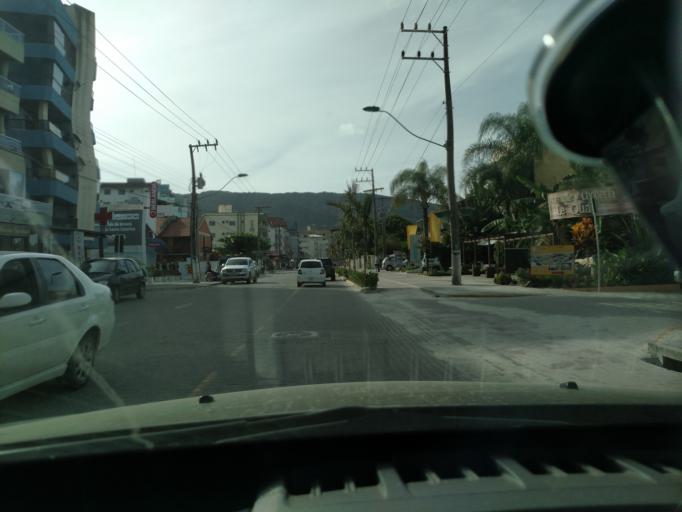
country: BR
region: Santa Catarina
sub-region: Porto Belo
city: Porto Belo
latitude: -27.1425
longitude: -48.5068
